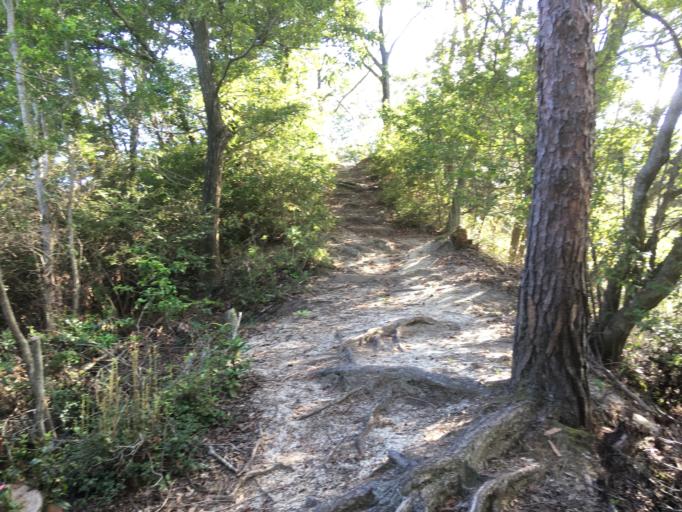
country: JP
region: Osaka
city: Neyagawa
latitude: 34.7460
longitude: 135.6844
